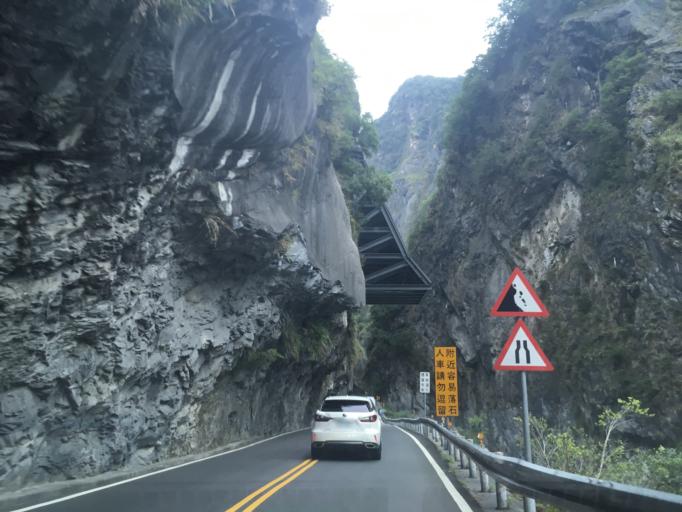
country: TW
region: Taiwan
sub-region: Hualien
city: Hualian
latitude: 24.1779
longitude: 121.5195
